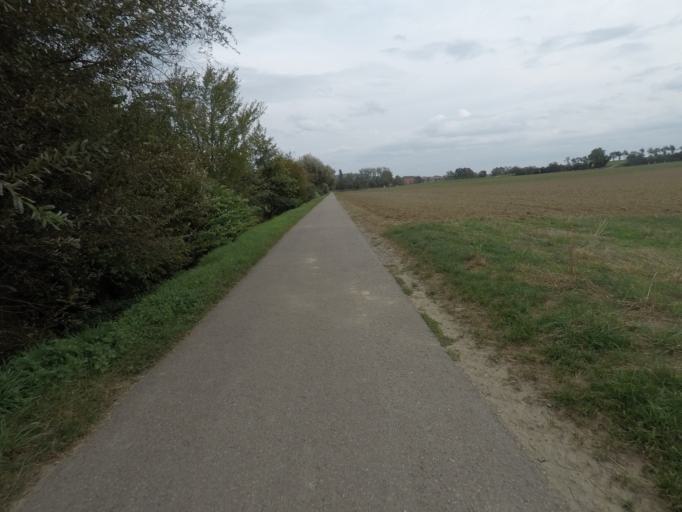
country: DE
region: Baden-Wuerttemberg
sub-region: Regierungsbezirk Stuttgart
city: Herrenberg
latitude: 48.5841
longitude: 8.8571
